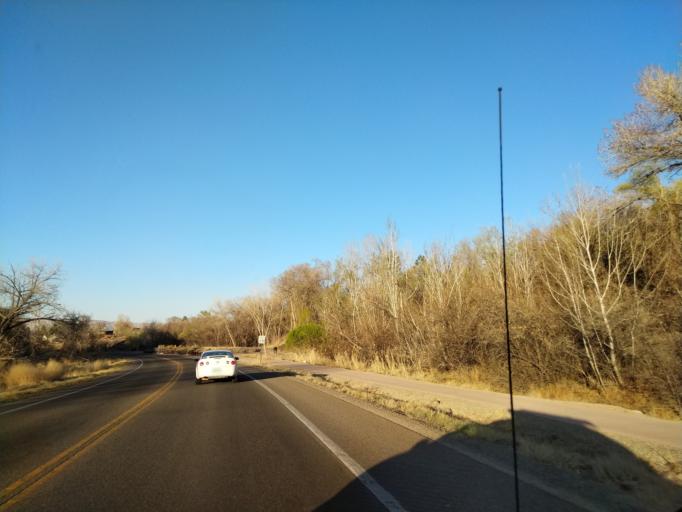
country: US
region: Colorado
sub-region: Mesa County
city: Grand Junction
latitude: 39.0584
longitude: -108.5919
